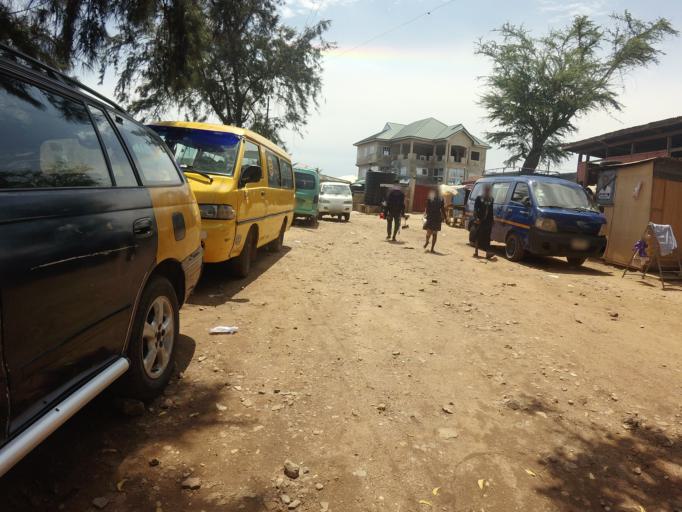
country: GH
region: Greater Accra
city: Accra
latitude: 5.5911
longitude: -0.2053
